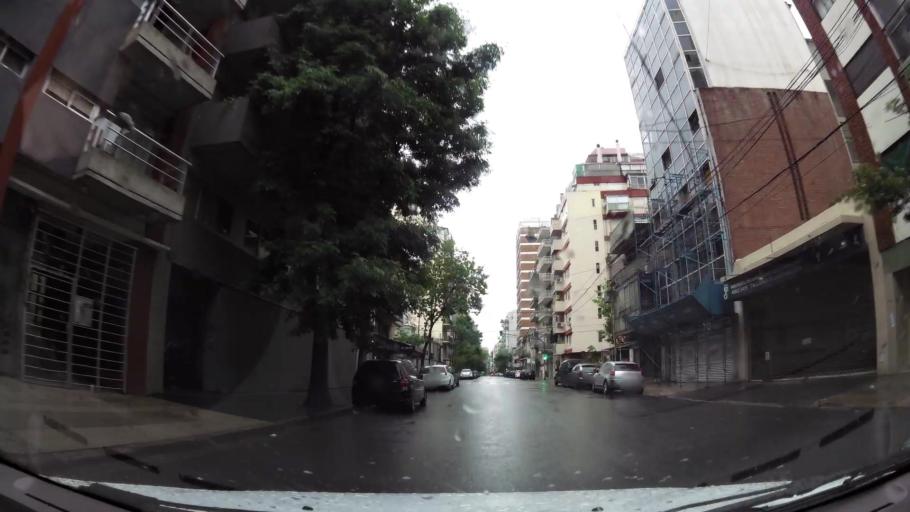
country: AR
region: Buenos Aires F.D.
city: Retiro
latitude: -34.5968
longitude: -58.4134
